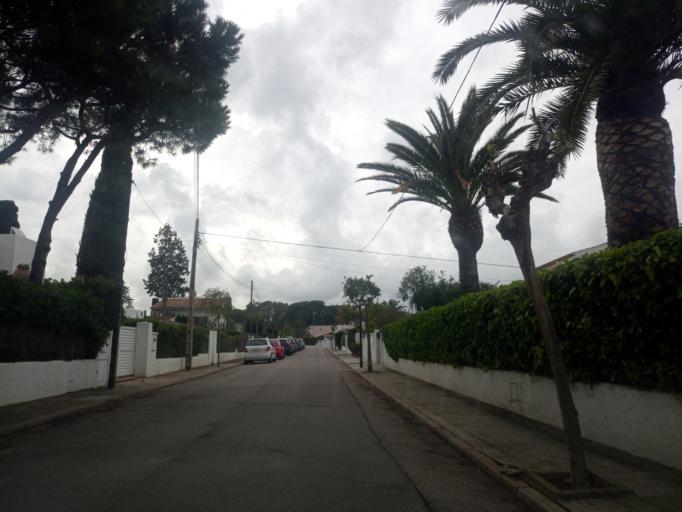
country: ES
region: Catalonia
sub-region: Provincia de Barcelona
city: Sant Pere de Ribes
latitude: 41.2544
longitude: 1.7777
